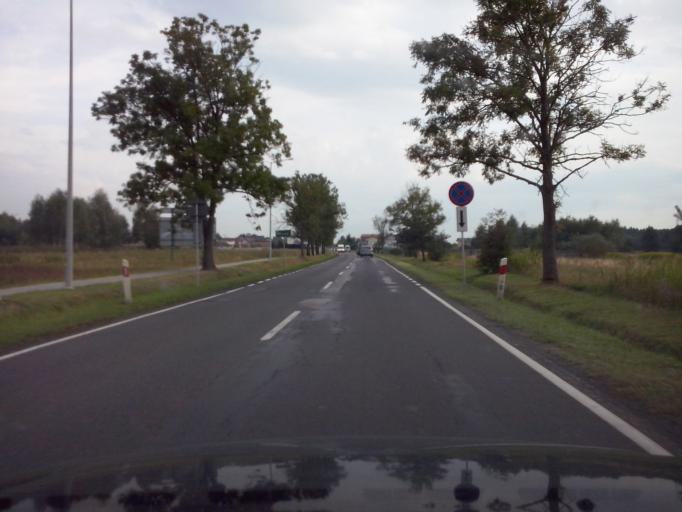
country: PL
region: Lublin Voivodeship
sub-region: Powiat bilgorajski
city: Bilgoraj
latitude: 50.5136
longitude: 22.7167
